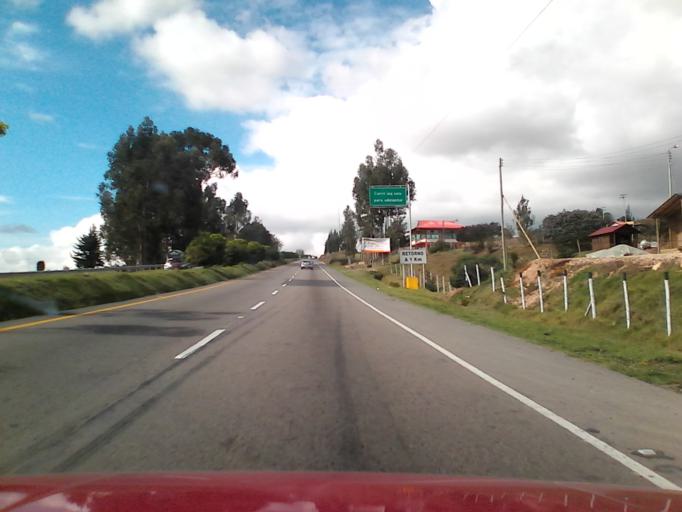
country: CO
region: Boyaca
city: Combita
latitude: 5.6335
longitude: -73.2959
